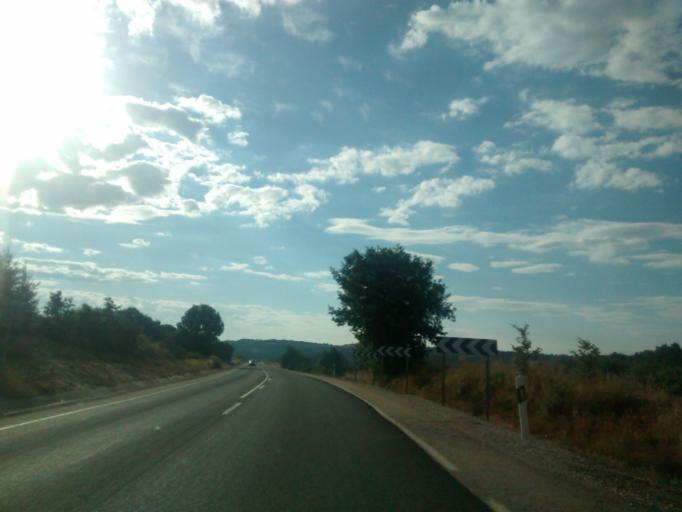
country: ES
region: Castille and Leon
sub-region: Provincia de Burgos
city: Basconcillos del Tozo
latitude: 42.6715
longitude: -3.9302
